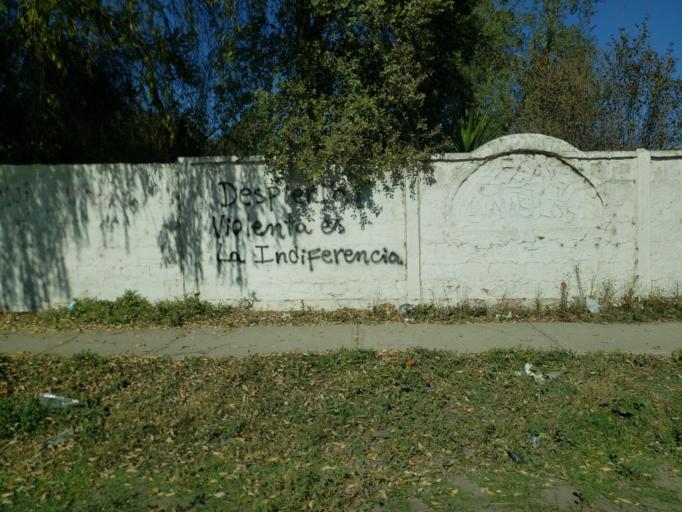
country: CL
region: Santiago Metropolitan
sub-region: Provincia de Talagante
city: El Monte
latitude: -33.6851
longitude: -71.0134
